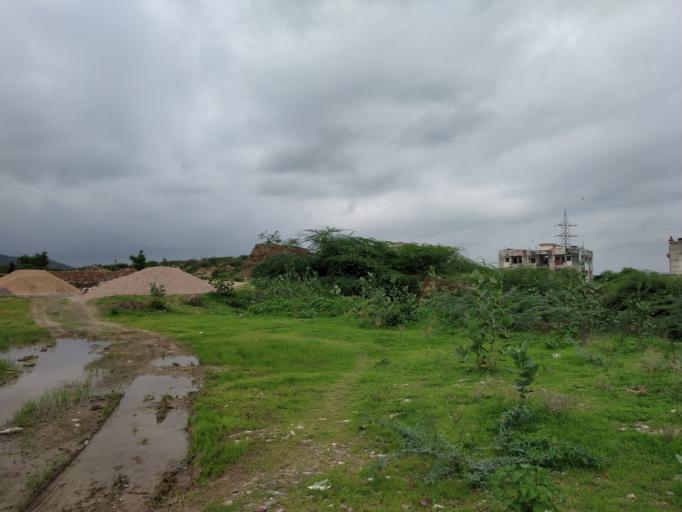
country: IN
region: Rajasthan
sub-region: Udaipur
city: Udaipur
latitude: 24.5914
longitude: 73.6543
